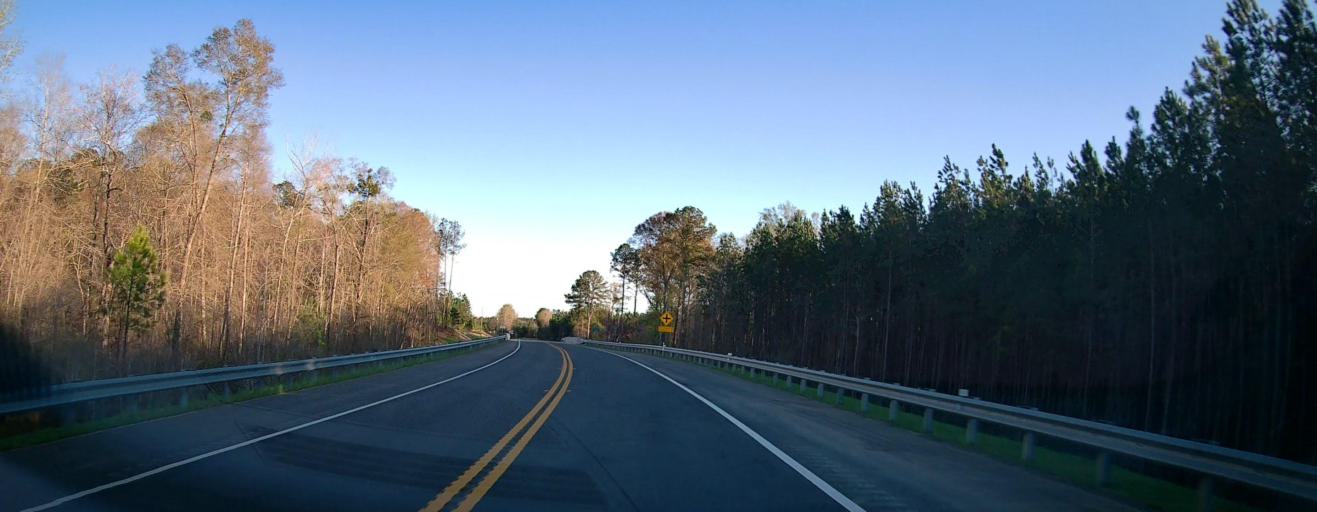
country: US
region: Georgia
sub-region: Wilcox County
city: Abbeville
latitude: 32.0852
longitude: -83.2916
